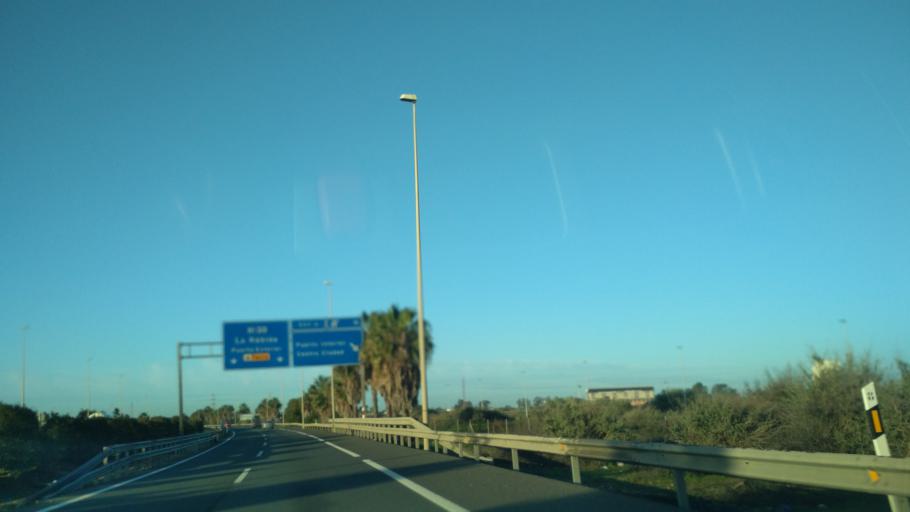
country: ES
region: Andalusia
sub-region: Provincia de Huelva
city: Huelva
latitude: 37.2497
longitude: -6.9393
